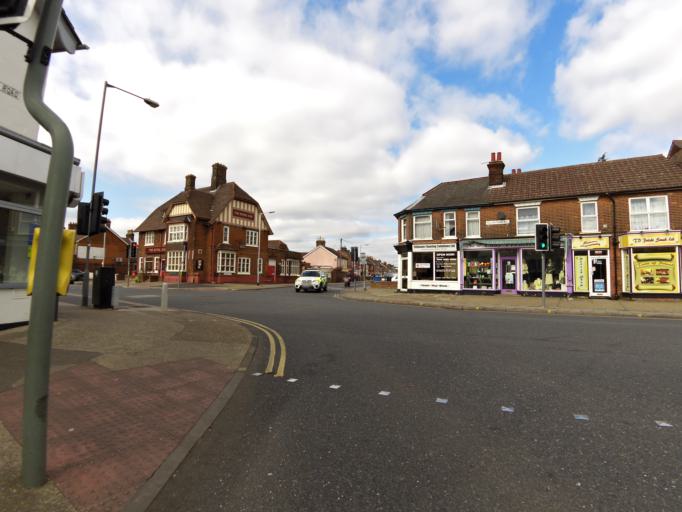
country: GB
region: England
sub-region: Suffolk
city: Ipswich
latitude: 52.0476
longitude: 1.1815
